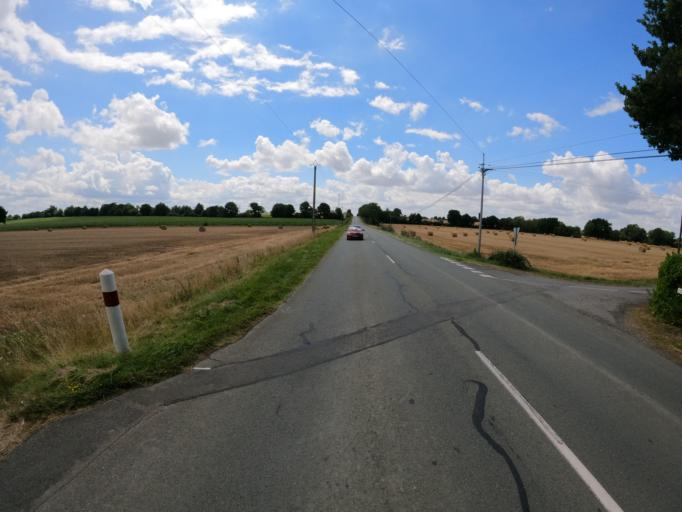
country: FR
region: Pays de la Loire
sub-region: Departement de Maine-et-Loire
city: Champigne
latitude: 47.6765
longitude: -0.5629
